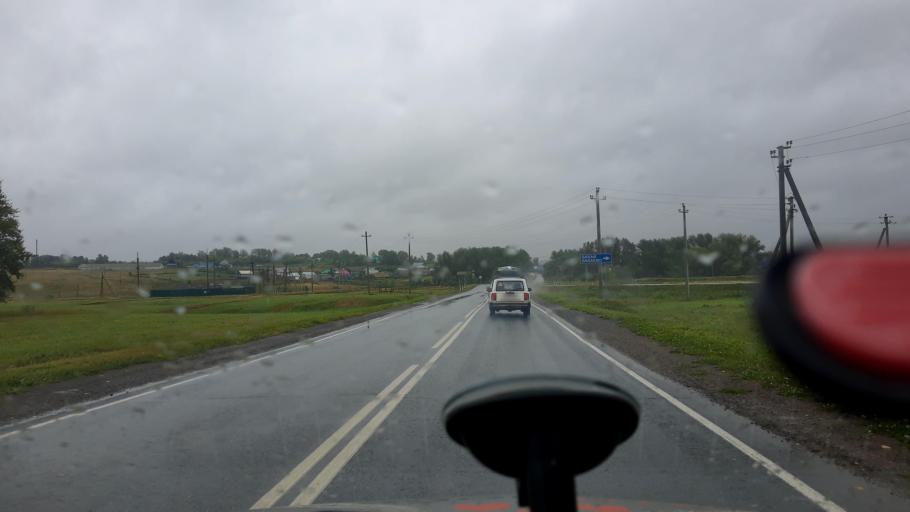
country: RU
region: Bashkortostan
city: Alekseyevka
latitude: 55.0558
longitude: 55.1185
